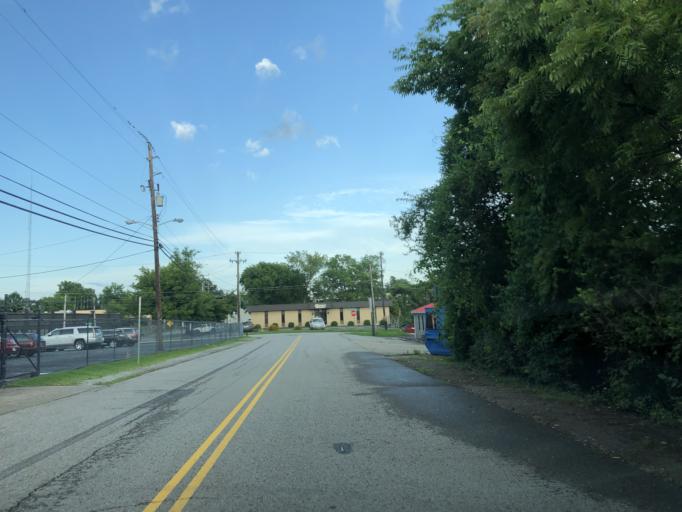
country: US
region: Tennessee
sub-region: Davidson County
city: Nashville
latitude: 36.1370
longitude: -86.7314
